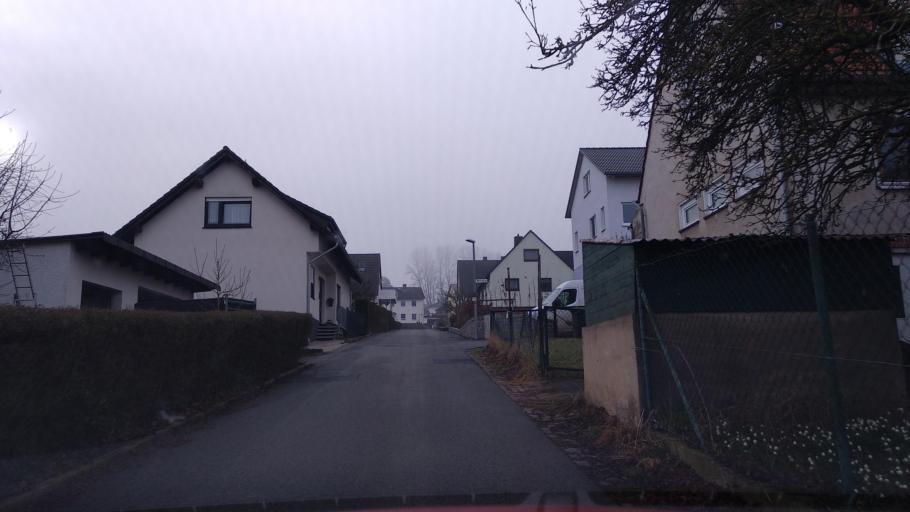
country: DE
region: Hesse
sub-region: Regierungsbezirk Kassel
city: Calden
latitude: 51.3612
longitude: 9.3837
